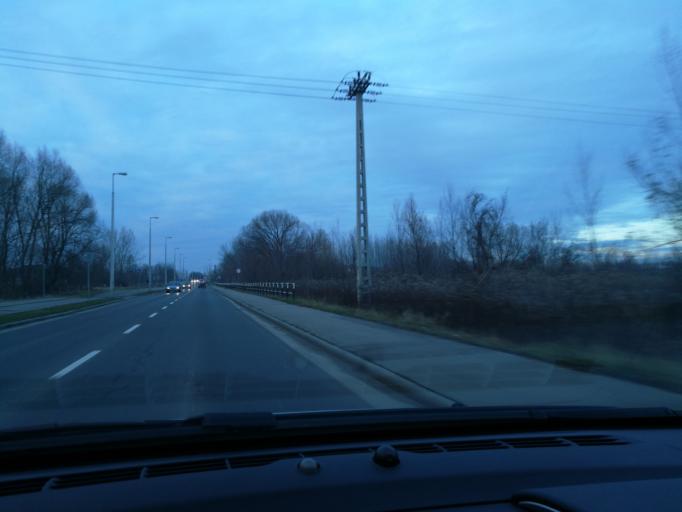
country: HU
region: Szabolcs-Szatmar-Bereg
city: Nyiregyhaza
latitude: 47.9660
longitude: 21.7425
